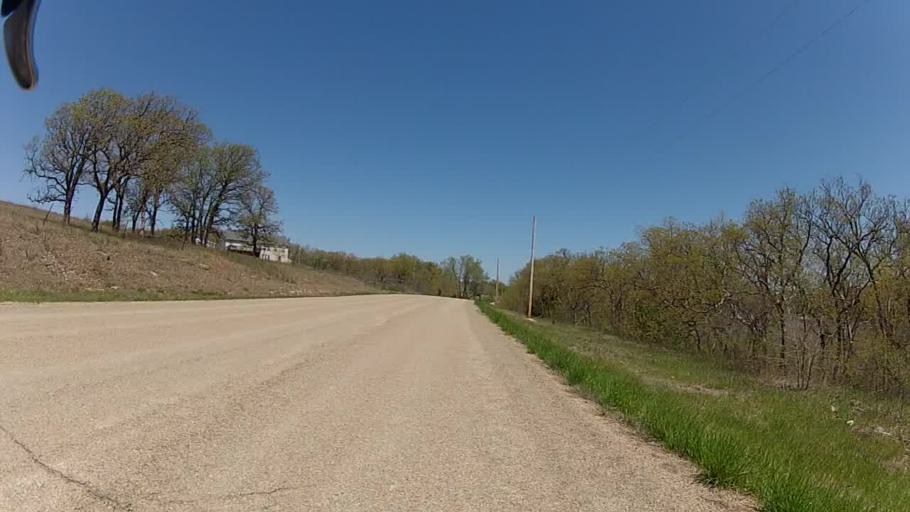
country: US
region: Kansas
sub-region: Riley County
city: Ogden
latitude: 38.9908
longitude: -96.5972
